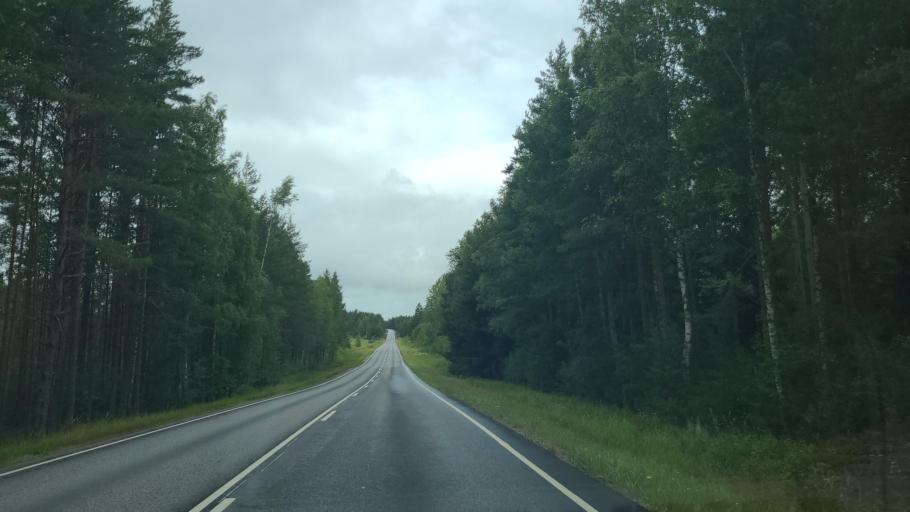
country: FI
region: Varsinais-Suomi
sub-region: Aboland-Turunmaa
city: Kimito
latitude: 60.2117
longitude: 22.6393
